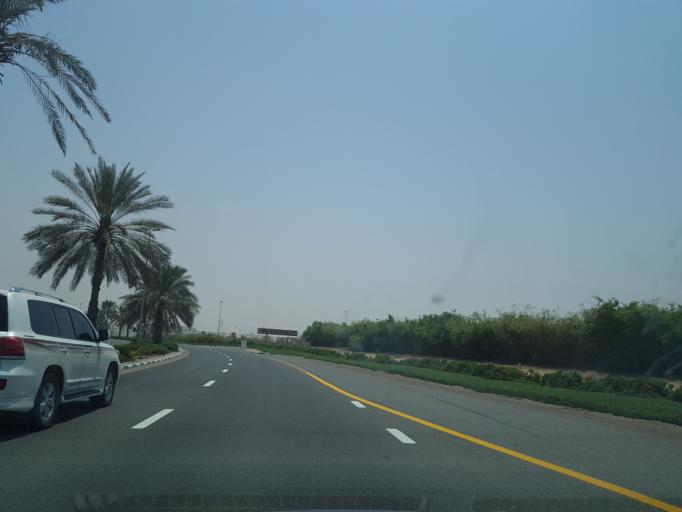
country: AE
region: Ash Shariqah
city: Sharjah
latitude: 25.1105
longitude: 55.3959
